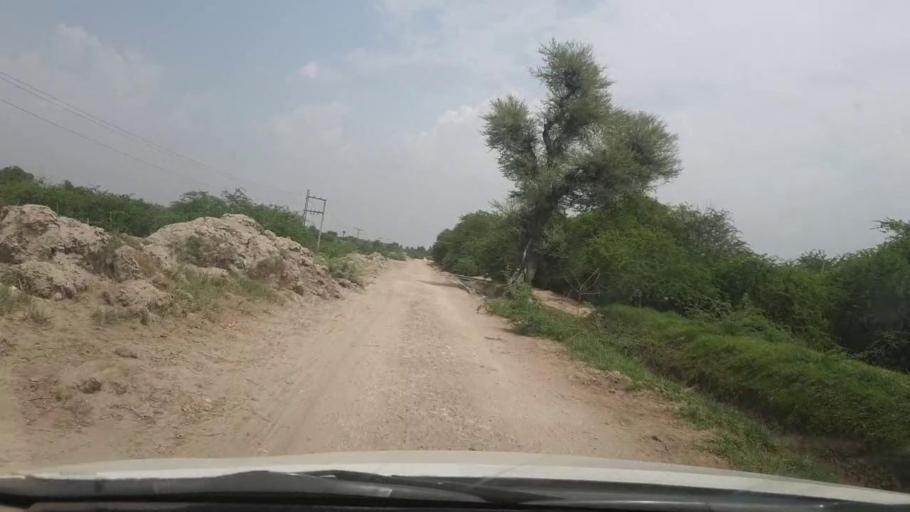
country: PK
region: Sindh
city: Khairpur
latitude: 27.3722
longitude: 68.9990
